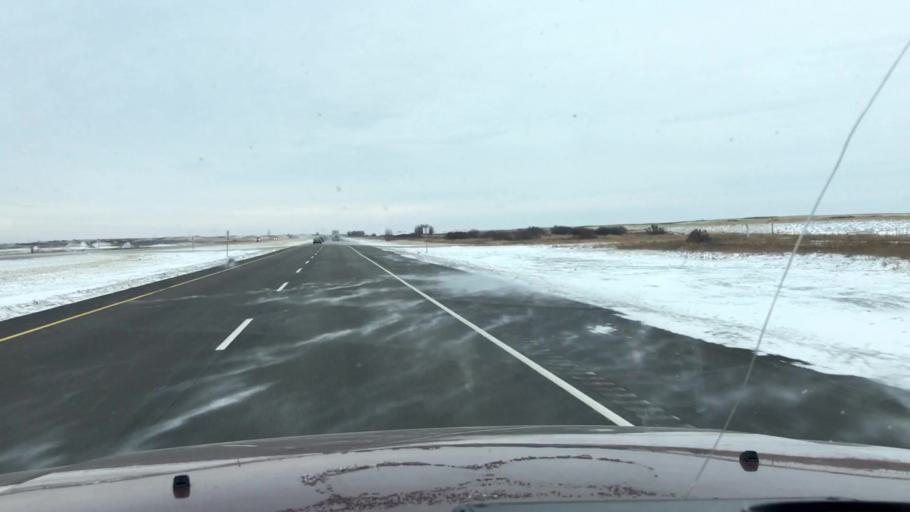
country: CA
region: Saskatchewan
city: Moose Jaw
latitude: 50.8930
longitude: -105.6277
